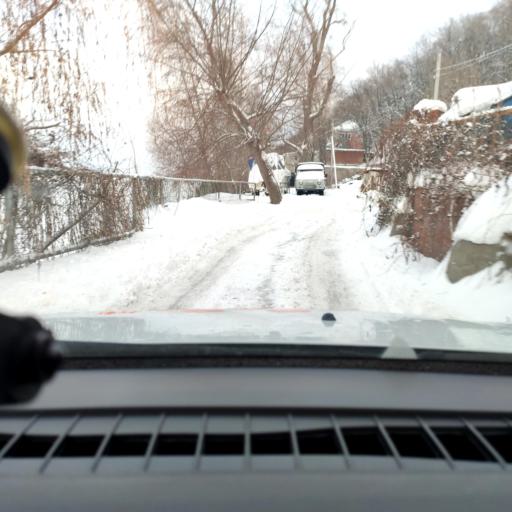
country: RU
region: Samara
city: Samara
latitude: 53.2841
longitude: 50.1897
